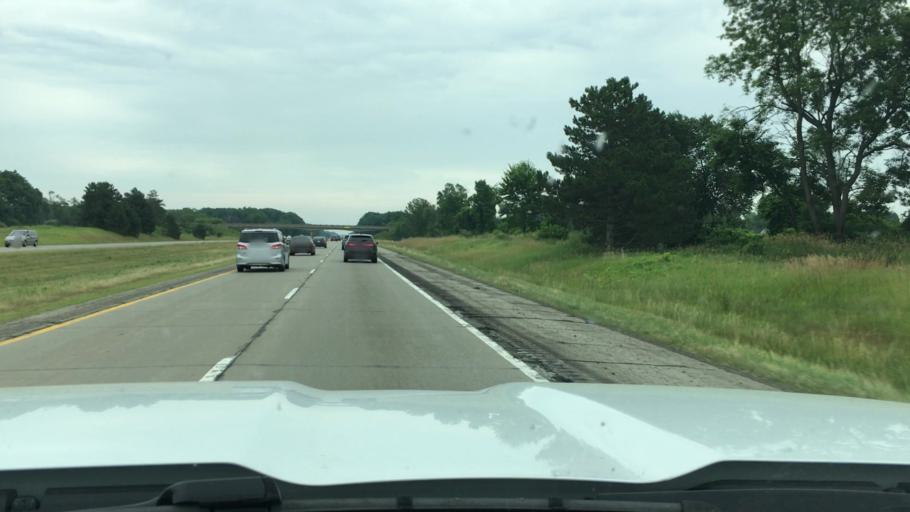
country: US
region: Michigan
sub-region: Ionia County
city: Portland
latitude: 42.8229
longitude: -84.8230
